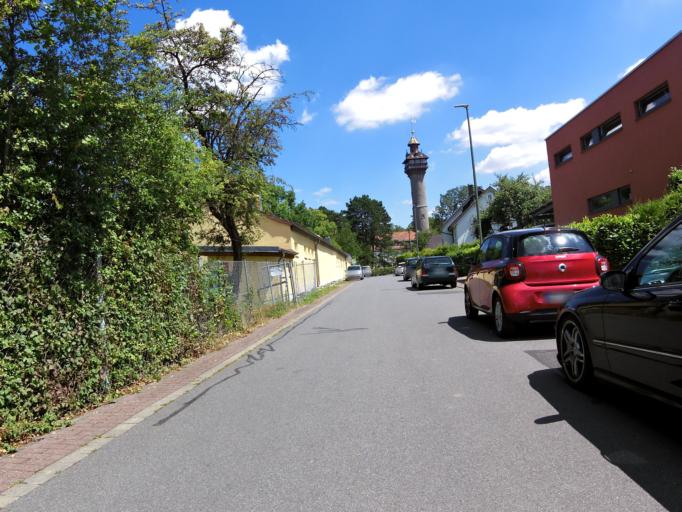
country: DE
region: Bavaria
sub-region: Regierungsbezirk Unterfranken
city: Hochberg
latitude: 49.7819
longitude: 9.9048
